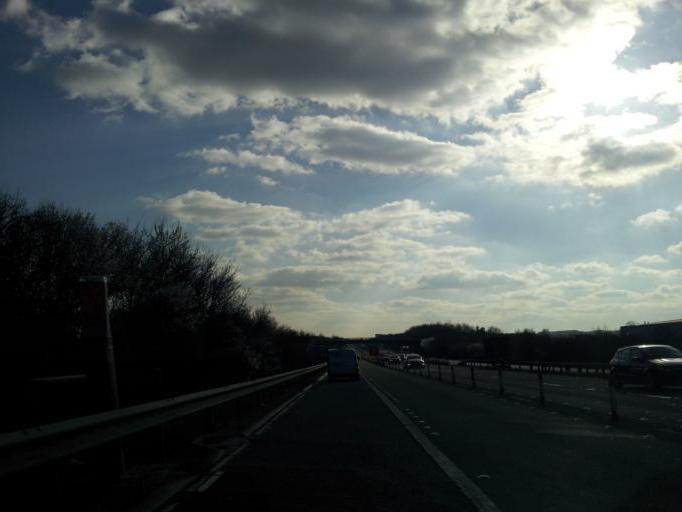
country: GB
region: England
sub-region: Somerset
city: Bridgwater
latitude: 51.1092
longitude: -2.9857
